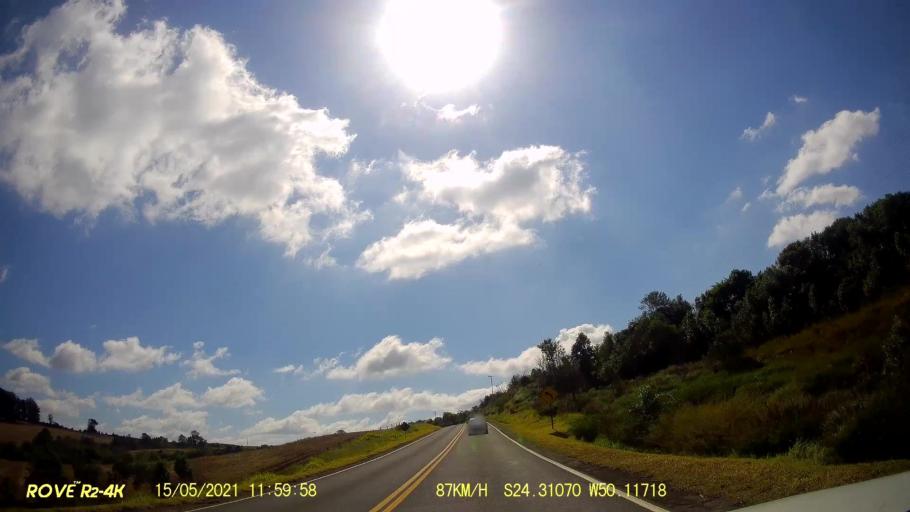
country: BR
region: Parana
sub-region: Pirai Do Sul
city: Pirai do Sul
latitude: -24.3107
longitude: -50.1172
